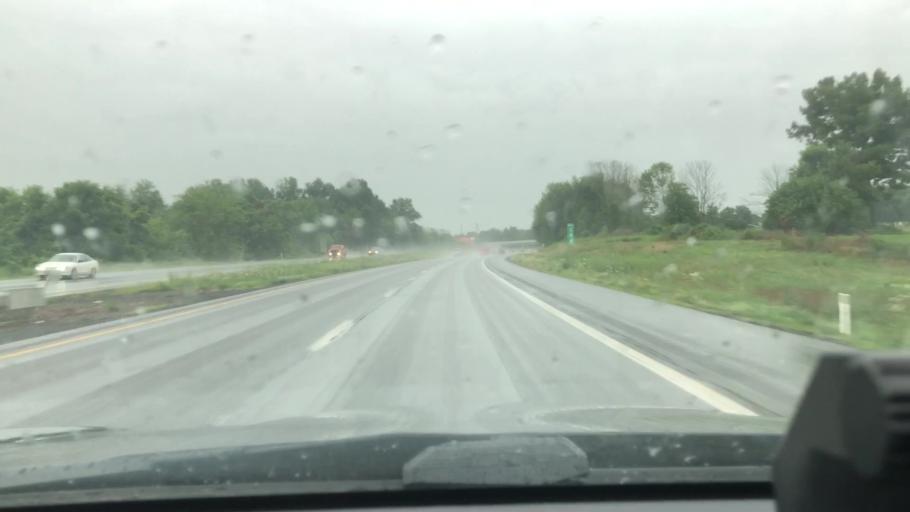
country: US
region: Pennsylvania
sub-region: Northampton County
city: Wind Gap
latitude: 40.8249
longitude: -75.2977
